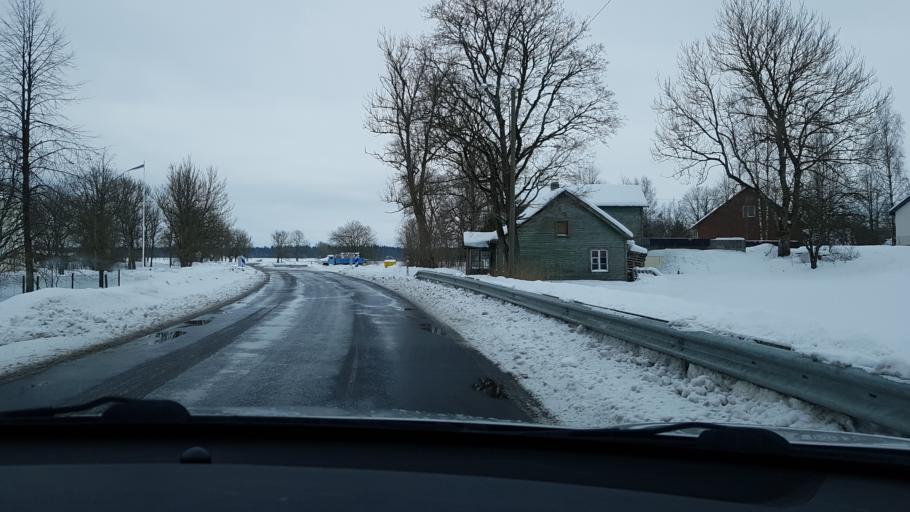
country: EE
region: Jaervamaa
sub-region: Jaerva-Jaani vald
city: Jarva-Jaani
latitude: 59.1413
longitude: 25.7523
